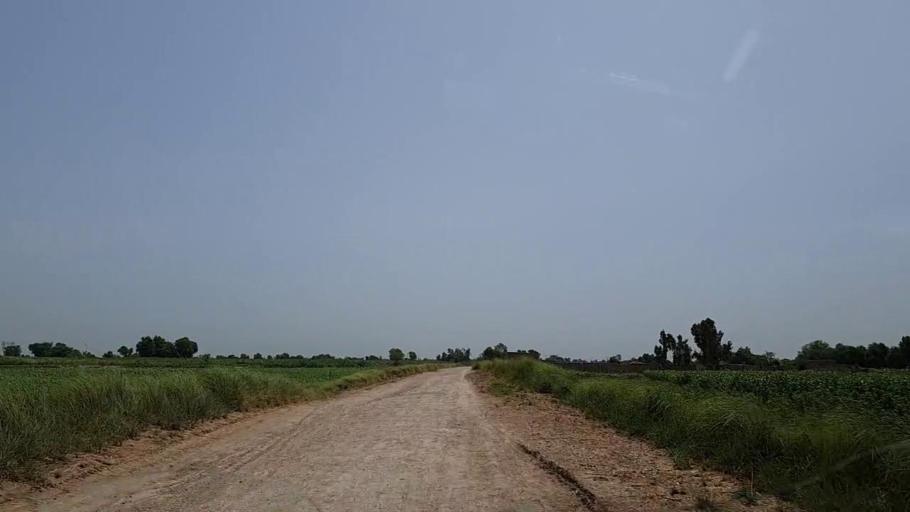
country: PK
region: Sindh
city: Naushahro Firoz
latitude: 26.8433
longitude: 67.9912
